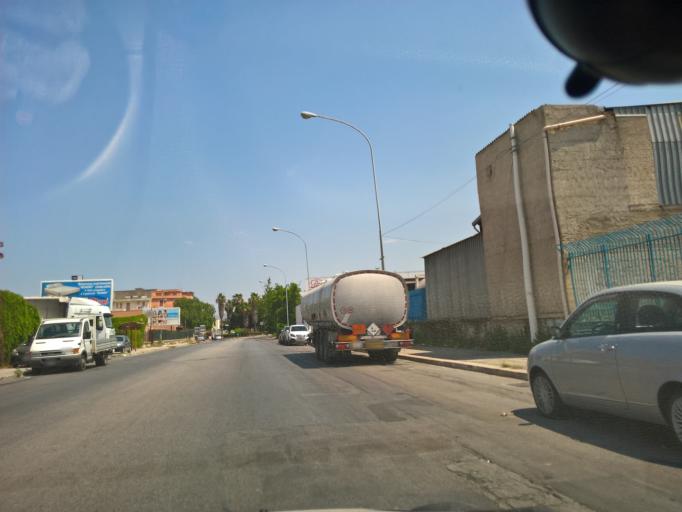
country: IT
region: Sicily
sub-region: Palermo
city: Ciaculli
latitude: 38.0943
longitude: 13.4015
